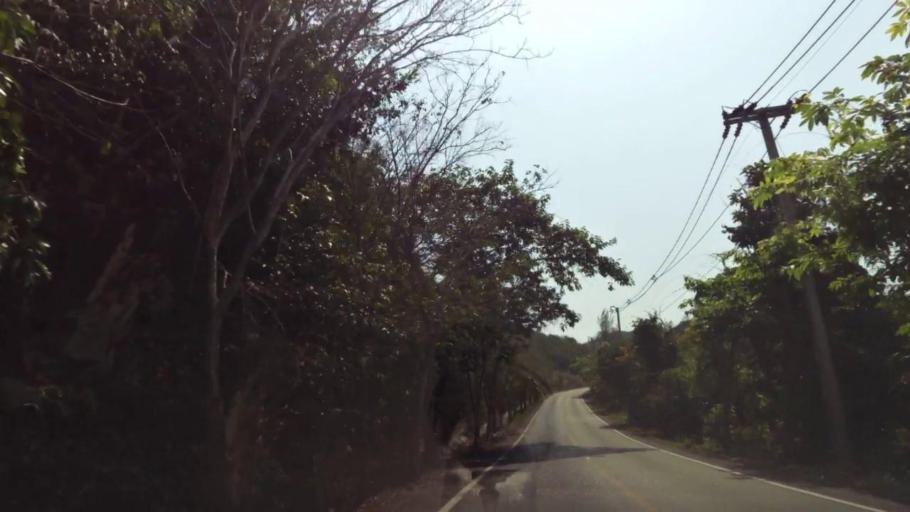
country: TH
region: Chanthaburi
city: Tha Mai
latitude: 12.5271
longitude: 101.9472
